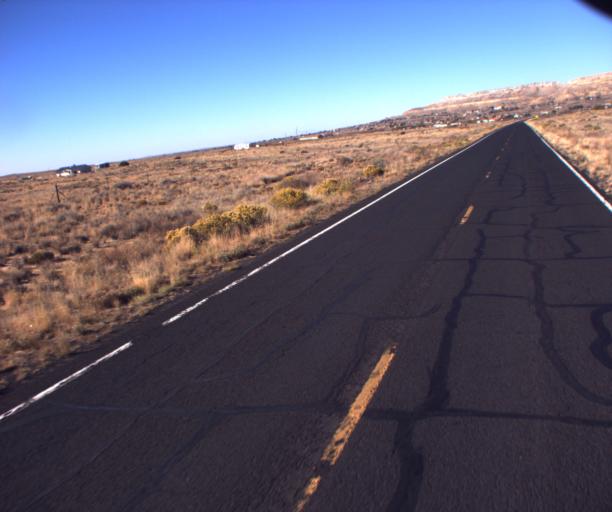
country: US
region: Arizona
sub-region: Navajo County
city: First Mesa
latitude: 35.8402
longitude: -110.3502
